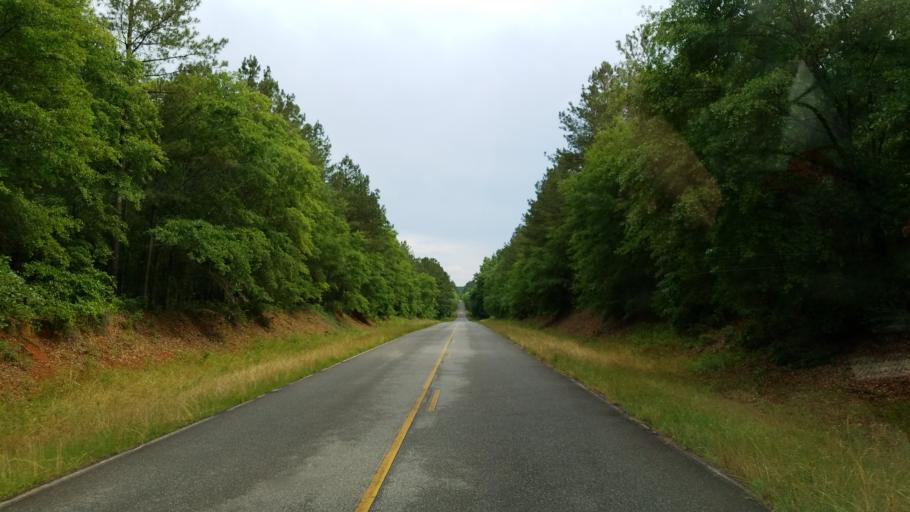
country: US
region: Georgia
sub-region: Dooly County
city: Unadilla
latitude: 32.3252
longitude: -83.7896
